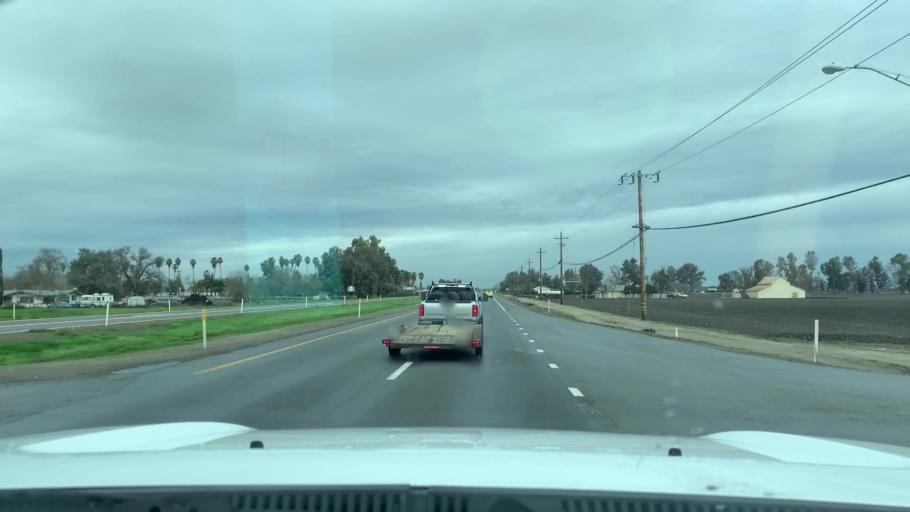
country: US
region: California
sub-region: Kings County
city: Lemoore
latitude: 36.3280
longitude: -119.8078
